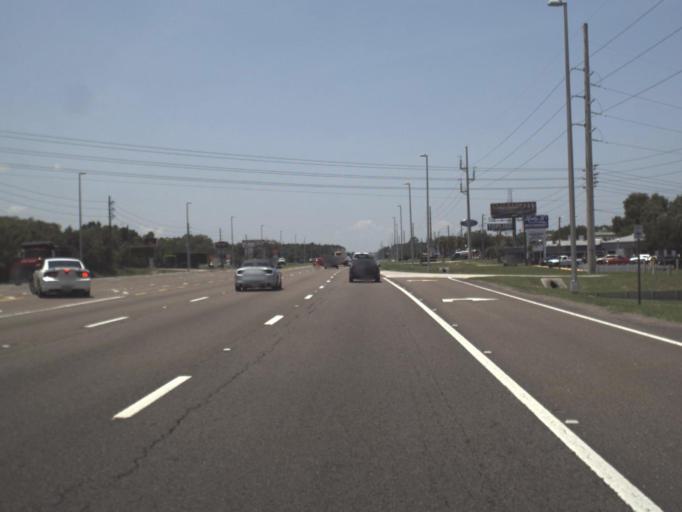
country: US
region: Florida
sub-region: Hernando County
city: Timber Pines
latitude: 28.4822
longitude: -82.6079
